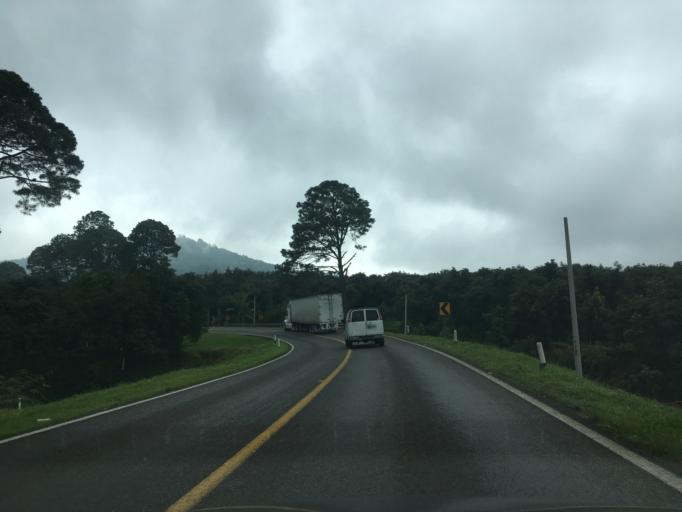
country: MX
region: Michoacan
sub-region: Uruapan
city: Toreo Bajo (El Toreo Bajo)
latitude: 19.4540
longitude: -101.9933
